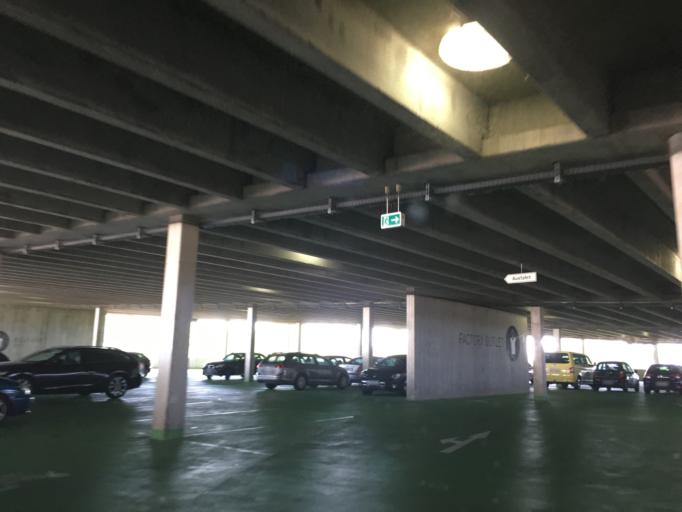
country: DE
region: Bavaria
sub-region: Regierungsbezirk Mittelfranken
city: Herzogenaurach
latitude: 49.5747
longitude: 10.9174
